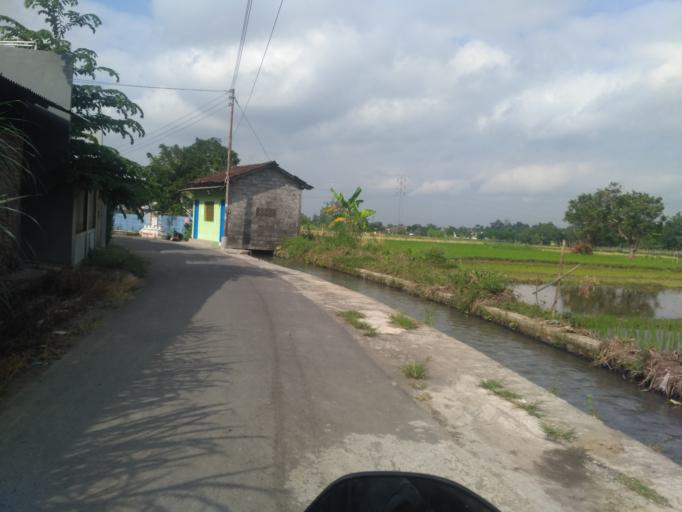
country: ID
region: Daerah Istimewa Yogyakarta
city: Melati
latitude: -7.7561
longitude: 110.3548
